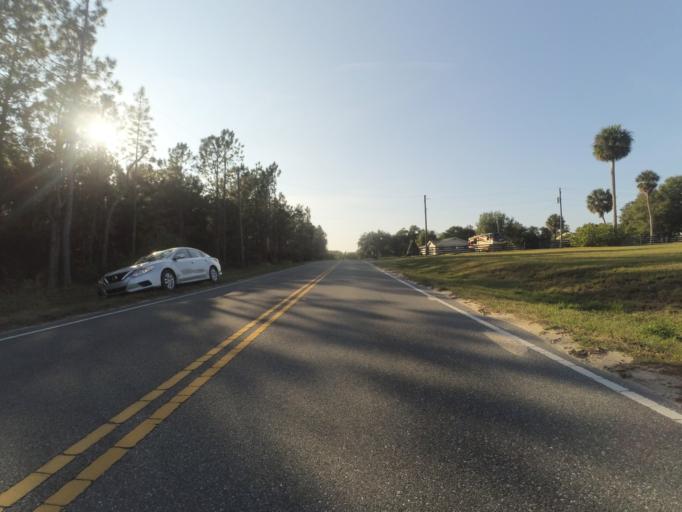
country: US
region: Florida
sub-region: Lake County
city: Umatilla
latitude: 28.9604
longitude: -81.6644
